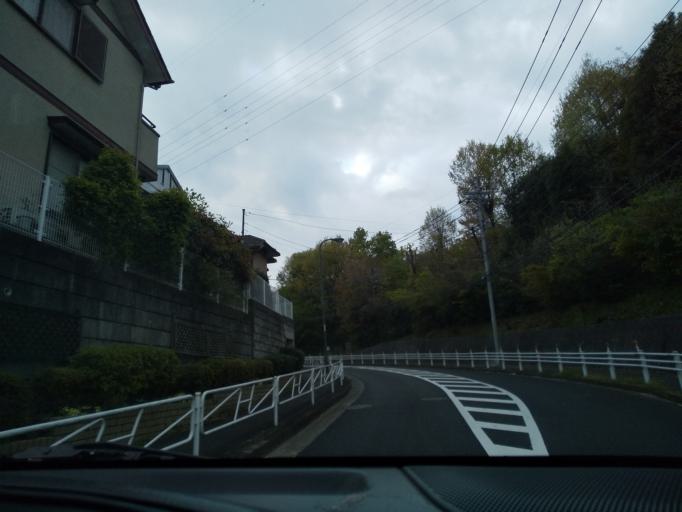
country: JP
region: Tokyo
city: Hino
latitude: 35.6046
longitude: 139.3776
